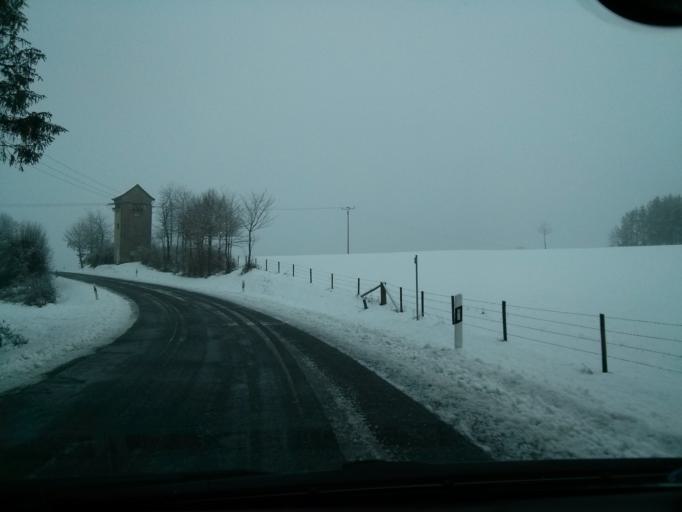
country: DE
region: Rheinland-Pfalz
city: Kirchsahr
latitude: 50.5037
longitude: 6.8432
